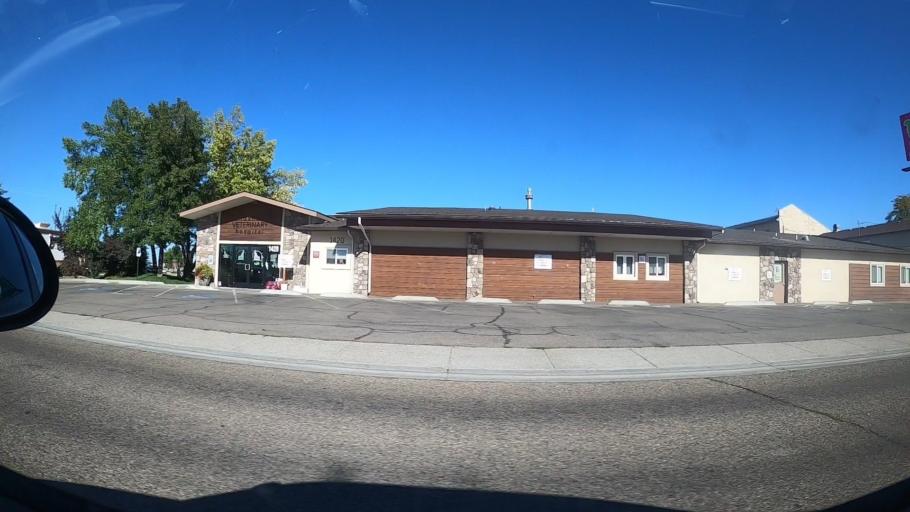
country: US
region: Idaho
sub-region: Canyon County
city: Nampa
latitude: 43.5948
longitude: -116.5931
